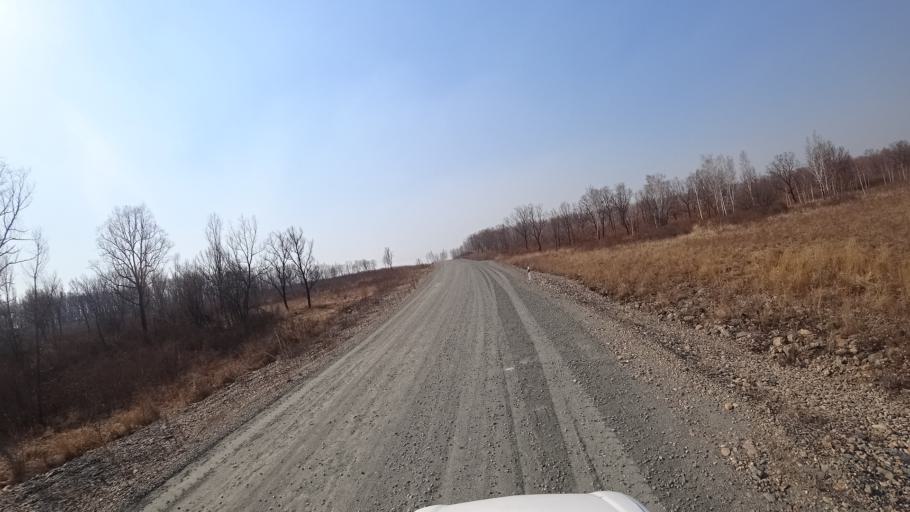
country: RU
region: Amur
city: Novobureyskiy
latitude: 49.8265
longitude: 129.9930
